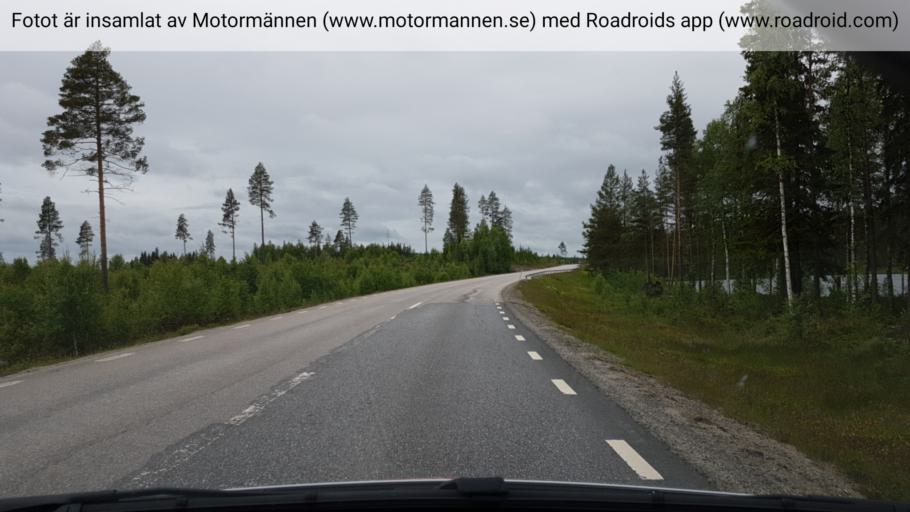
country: SE
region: Vaesterbotten
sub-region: Vindelns Kommun
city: Vindeln
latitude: 64.0566
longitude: 19.6508
